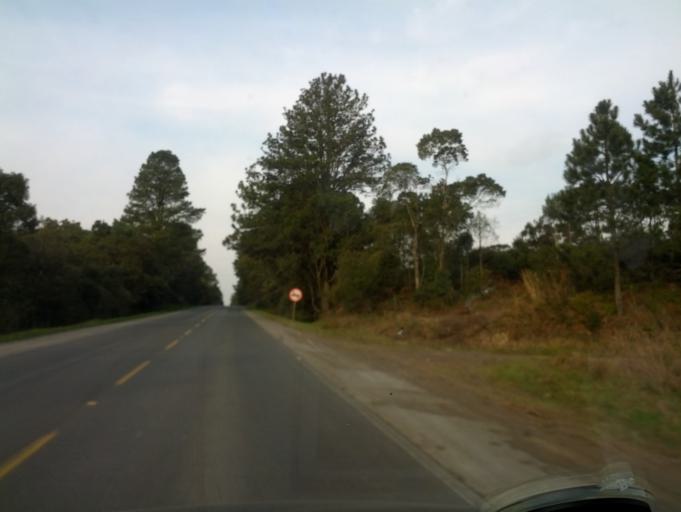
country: BR
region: Santa Catarina
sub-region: Otacilio Costa
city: Otacilio Costa
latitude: -27.3051
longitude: -50.1002
